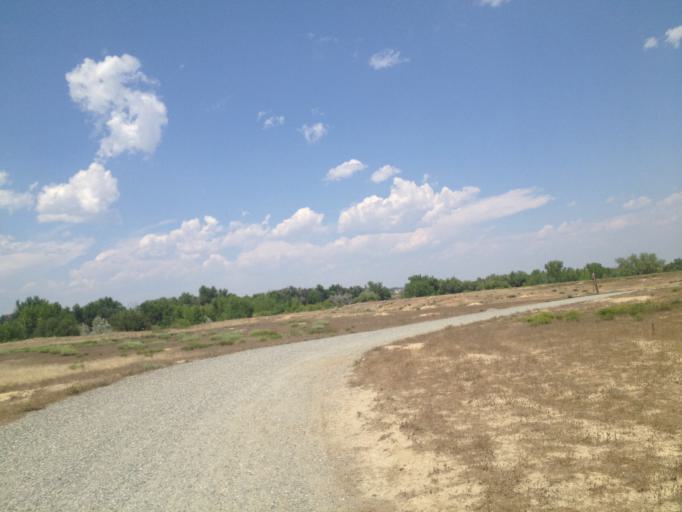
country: US
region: Colorado
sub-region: Boulder County
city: Lafayette
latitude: 39.9876
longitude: -105.0608
